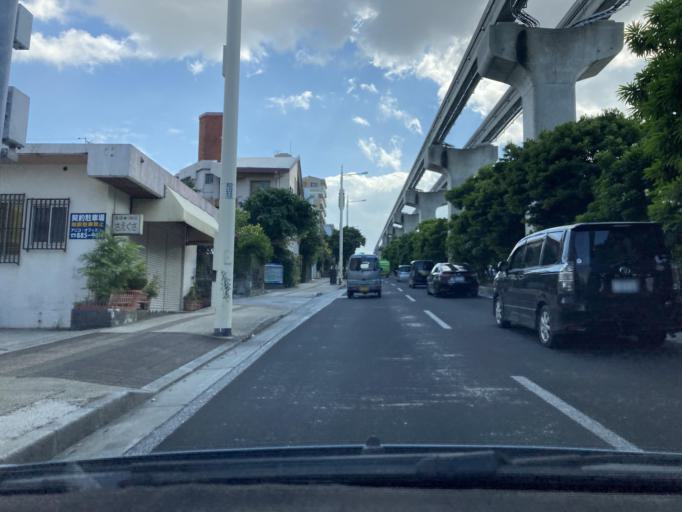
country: JP
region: Okinawa
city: Naha-shi
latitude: 26.2232
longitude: 127.7207
